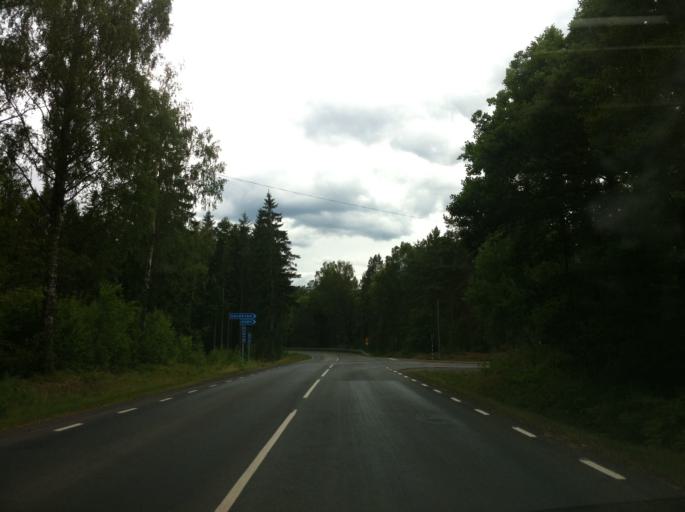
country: SE
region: Skane
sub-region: Osby Kommun
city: Lonsboda
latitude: 56.3774
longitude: 14.2557
